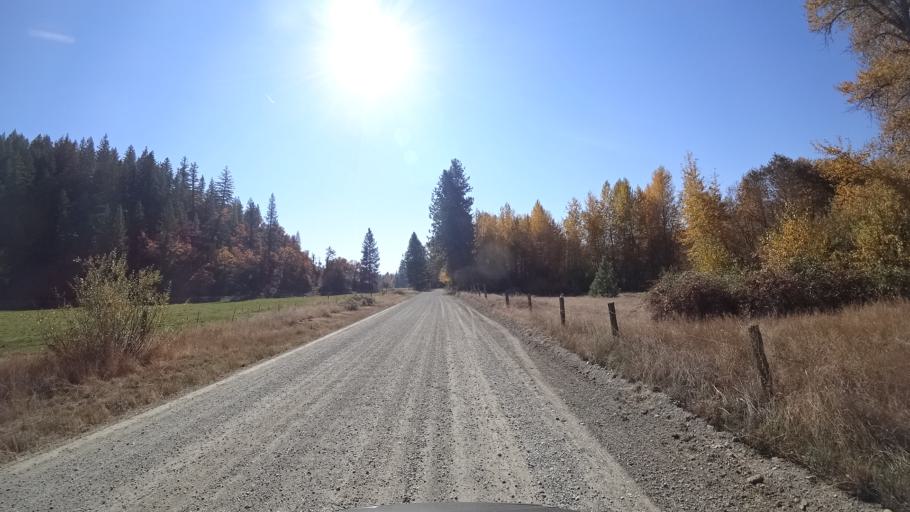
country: US
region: California
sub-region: Siskiyou County
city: Yreka
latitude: 41.6207
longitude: -122.9651
